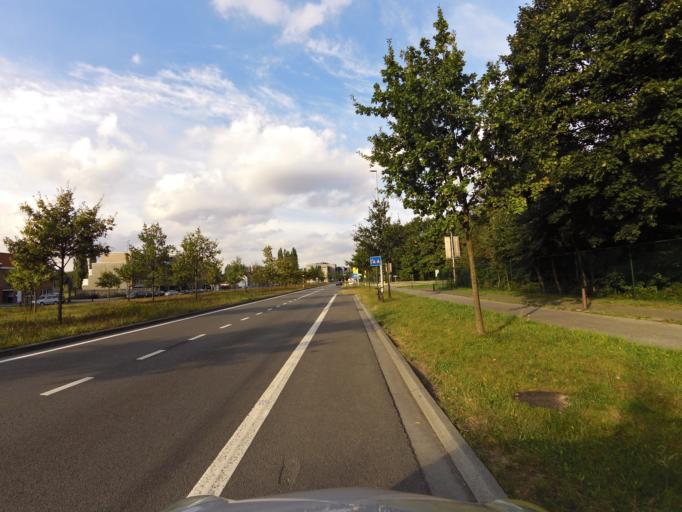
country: BE
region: Flanders
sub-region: Provincie Oost-Vlaanderen
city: Gent
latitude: 51.0109
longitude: 3.7036
